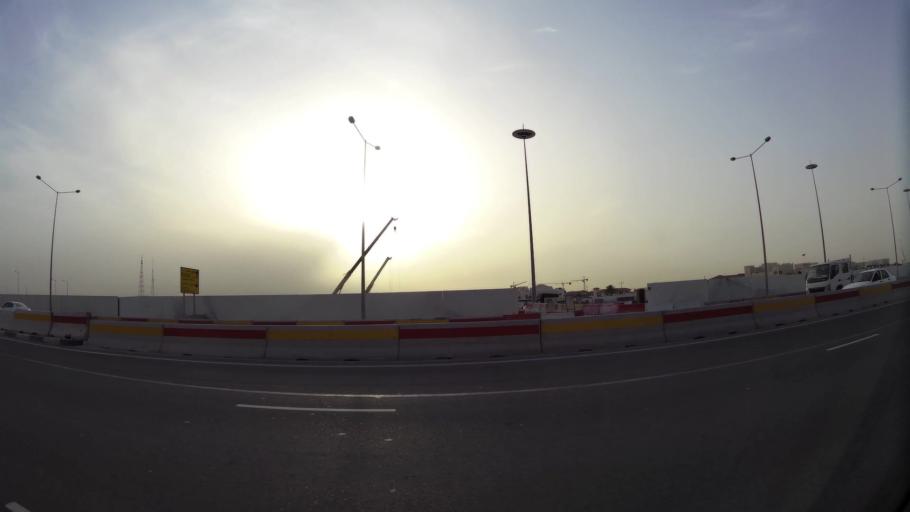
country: QA
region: Baladiyat ad Dawhah
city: Doha
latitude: 25.3413
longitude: 51.5212
